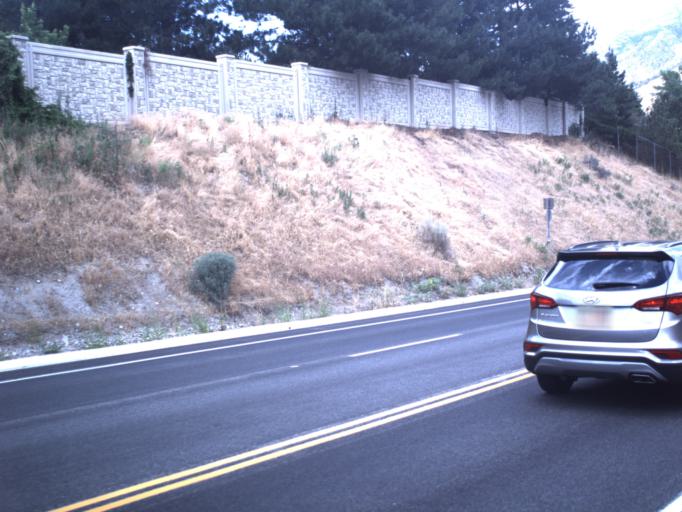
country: US
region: Utah
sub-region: Salt Lake County
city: Cottonwood Heights
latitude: 40.6131
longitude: -111.7895
